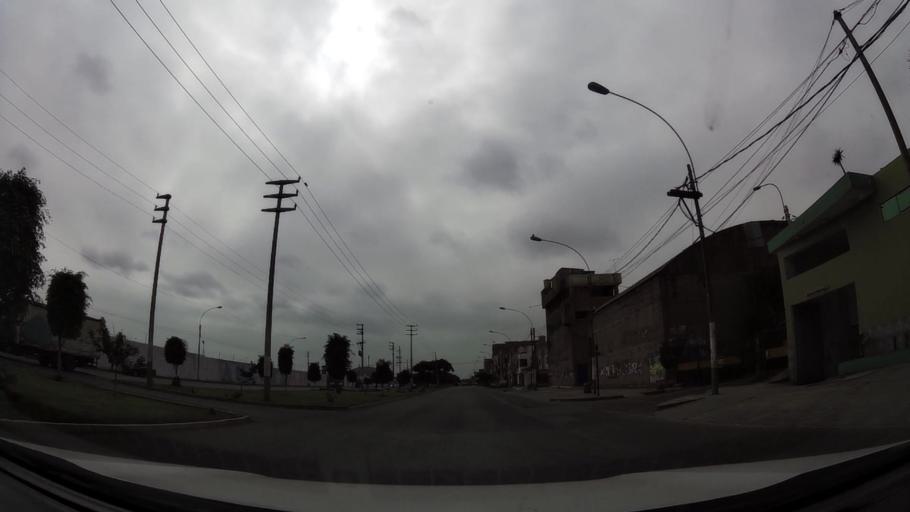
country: PE
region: Callao
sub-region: Callao
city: Callao
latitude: -12.0077
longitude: -77.1070
